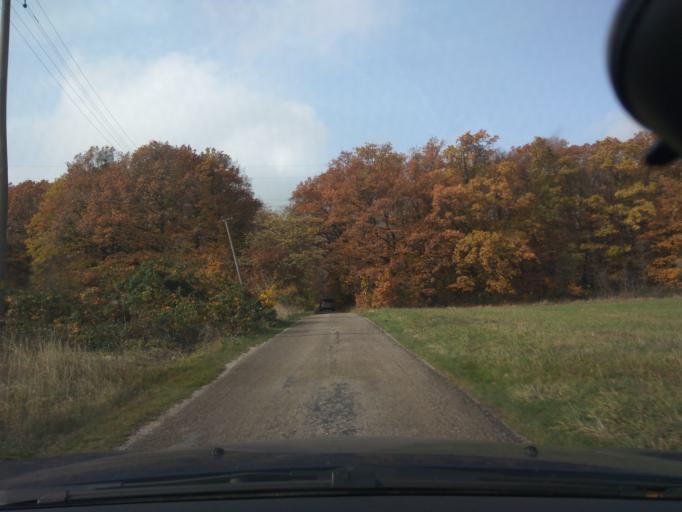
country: SK
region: Trnavsky
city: Vrbove
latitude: 48.6816
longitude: 17.7198
